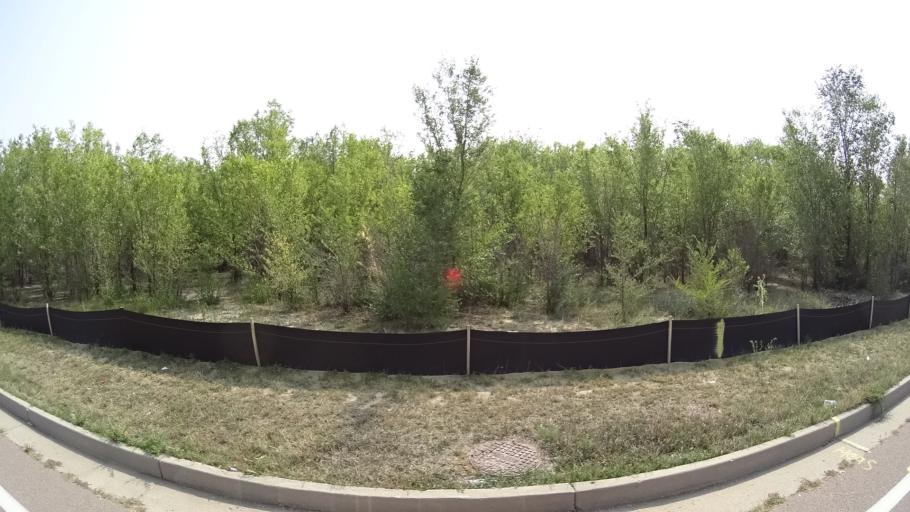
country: US
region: Colorado
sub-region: El Paso County
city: Stratmoor
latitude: 38.8098
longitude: -104.7557
